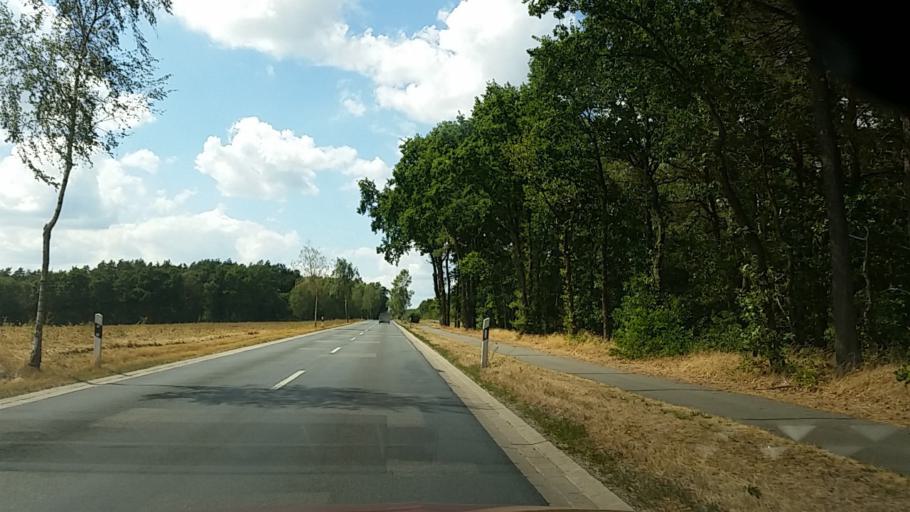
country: DE
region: Lower Saxony
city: Hankensbuttel
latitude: 52.7193
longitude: 10.6058
